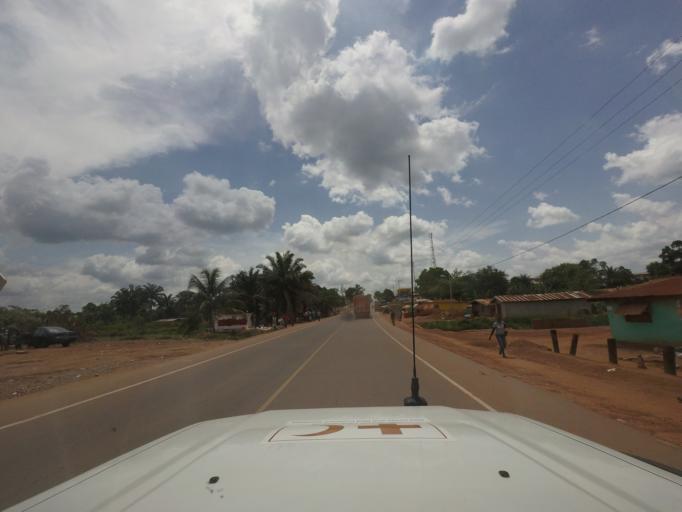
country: LR
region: Nimba
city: Sanniquellie
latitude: 7.2317
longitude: -8.9914
